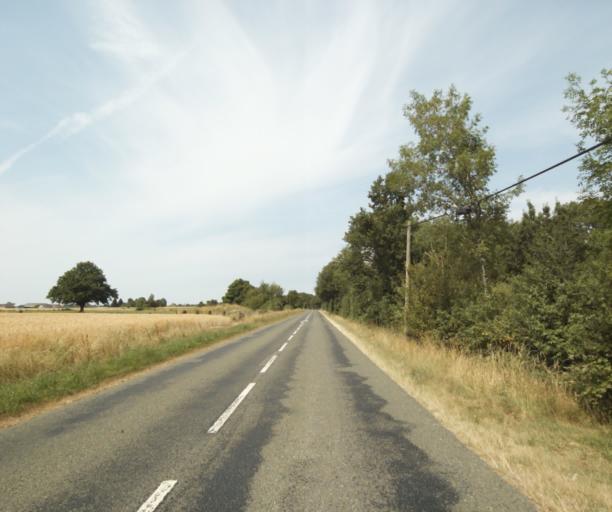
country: FR
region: Centre
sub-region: Departement d'Eure-et-Loir
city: Unverre
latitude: 48.1946
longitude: 1.0777
